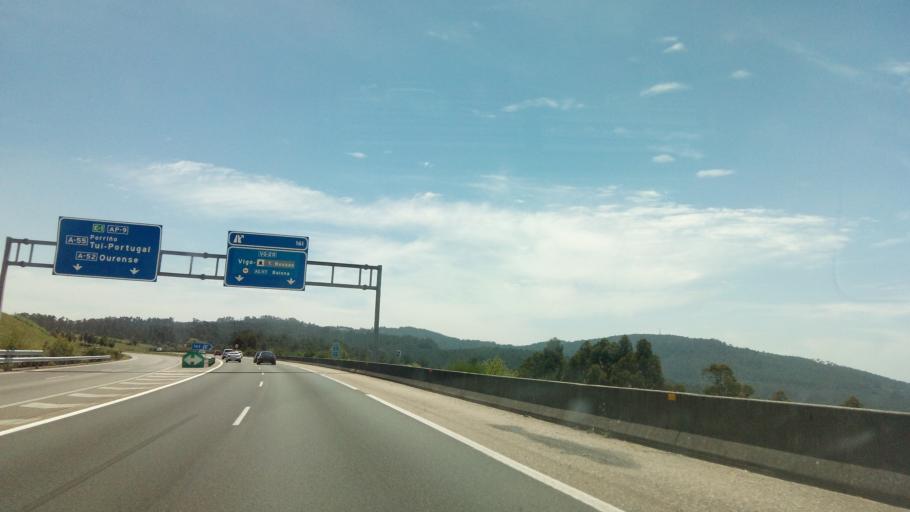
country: ES
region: Galicia
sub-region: Provincia de Pontevedra
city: Vigo
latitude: 42.2027
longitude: -8.6688
